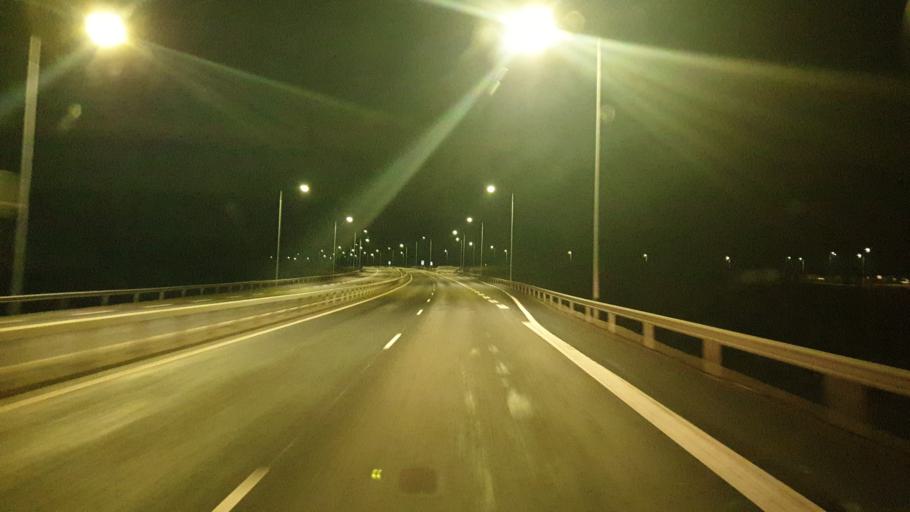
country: FI
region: Central Finland
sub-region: AEaenekoski
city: AEaenekoski
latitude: 62.6062
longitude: 25.6899
